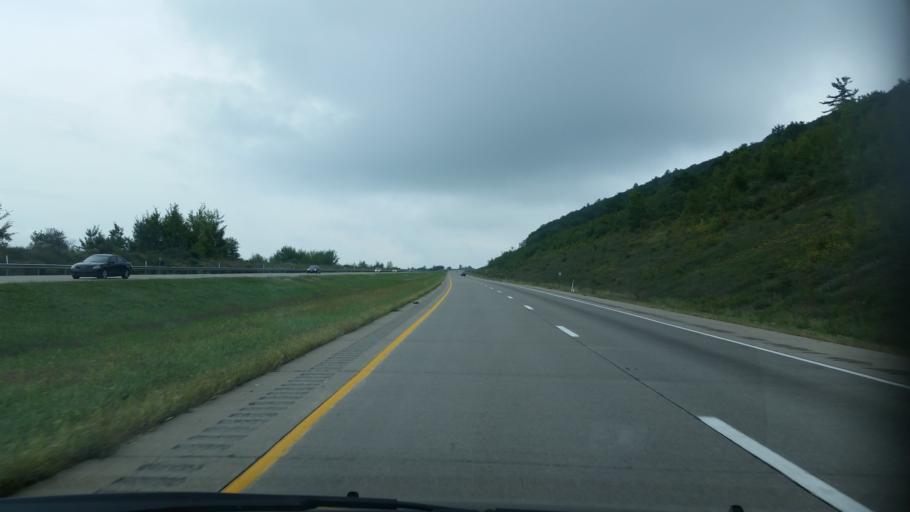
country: US
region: Pennsylvania
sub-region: Centre County
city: Stormstown
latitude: 40.8256
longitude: -77.9979
